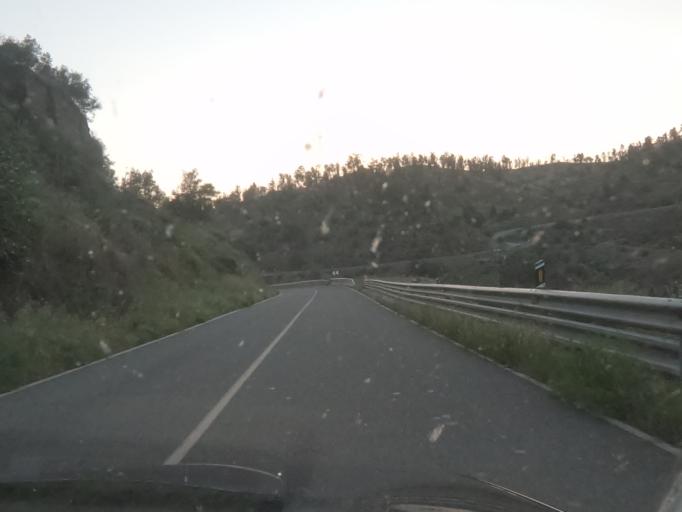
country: ES
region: Extremadura
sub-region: Provincia de Caceres
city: Alcantara
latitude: 39.7227
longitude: -6.8881
